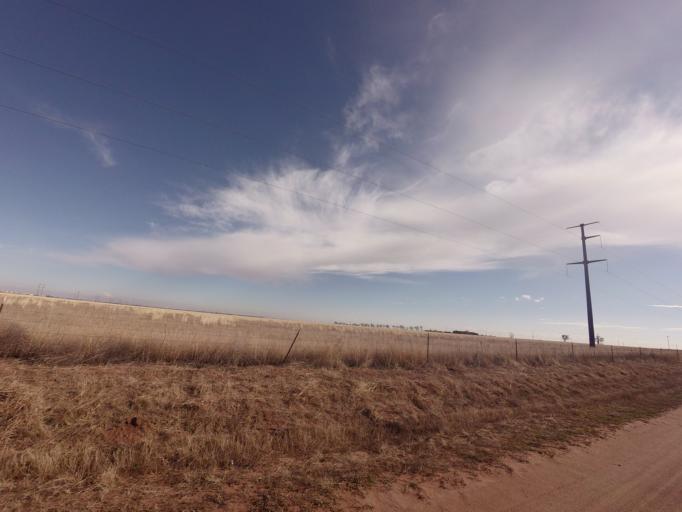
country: US
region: New Mexico
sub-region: Curry County
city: Texico
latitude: 34.3961
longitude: -103.1258
